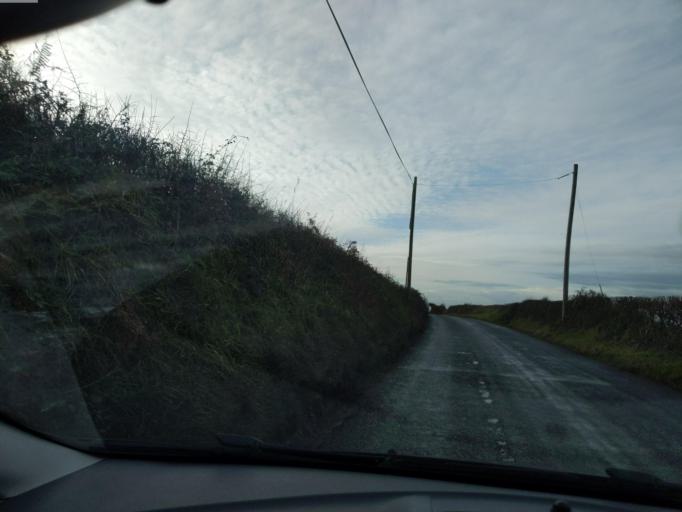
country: GB
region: England
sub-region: Cornwall
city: Camelford
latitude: 50.6949
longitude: -4.6721
